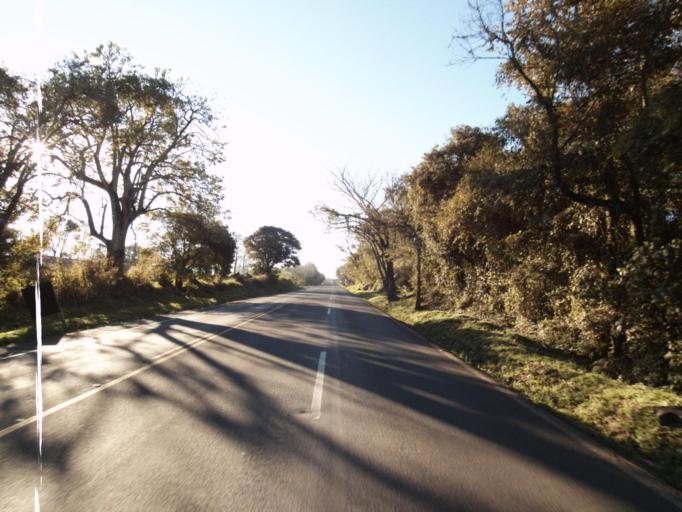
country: BR
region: Santa Catarina
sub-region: Chapeco
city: Chapeco
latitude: -26.9078
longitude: -52.8666
